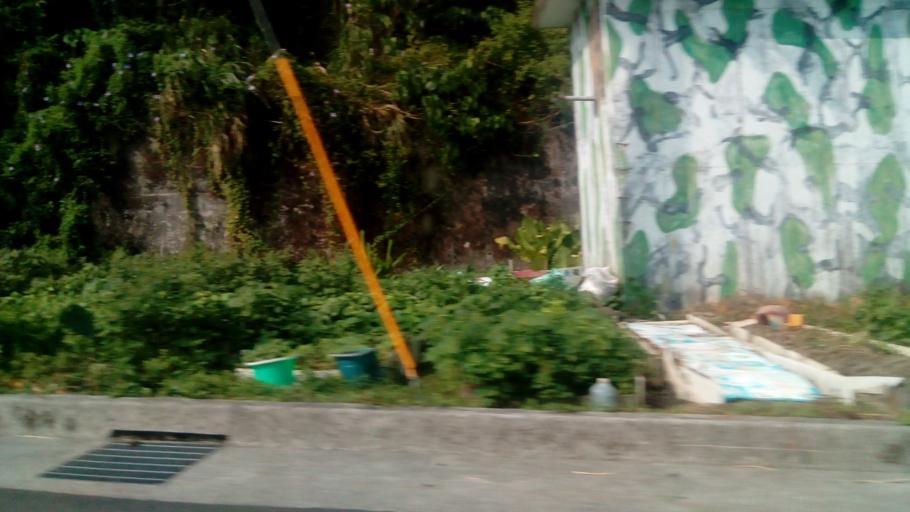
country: TW
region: Taiwan
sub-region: Yilan
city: Yilan
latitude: 24.5872
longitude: 121.8632
